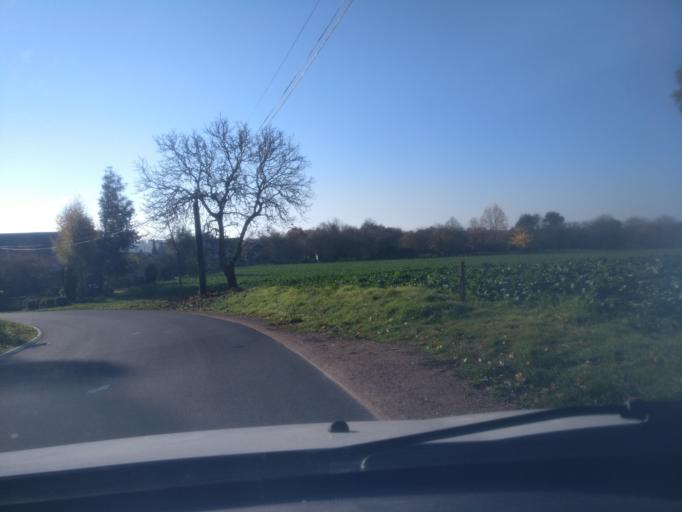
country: FR
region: Brittany
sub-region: Departement d'Ille-et-Vilaine
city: Guichen
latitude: 48.0087
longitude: -1.7916
